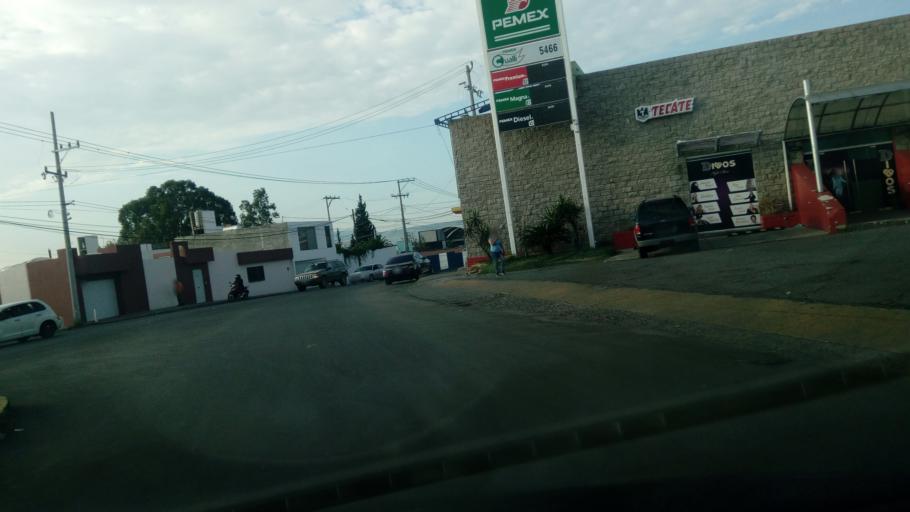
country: MX
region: Durango
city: Victoria de Durango
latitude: 24.0156
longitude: -104.6768
